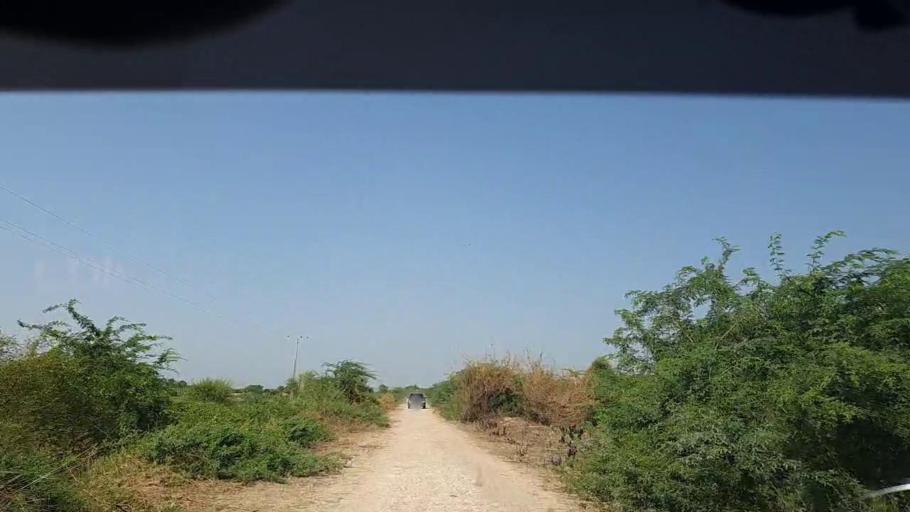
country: PK
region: Sindh
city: Badin
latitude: 24.4652
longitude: 68.7797
